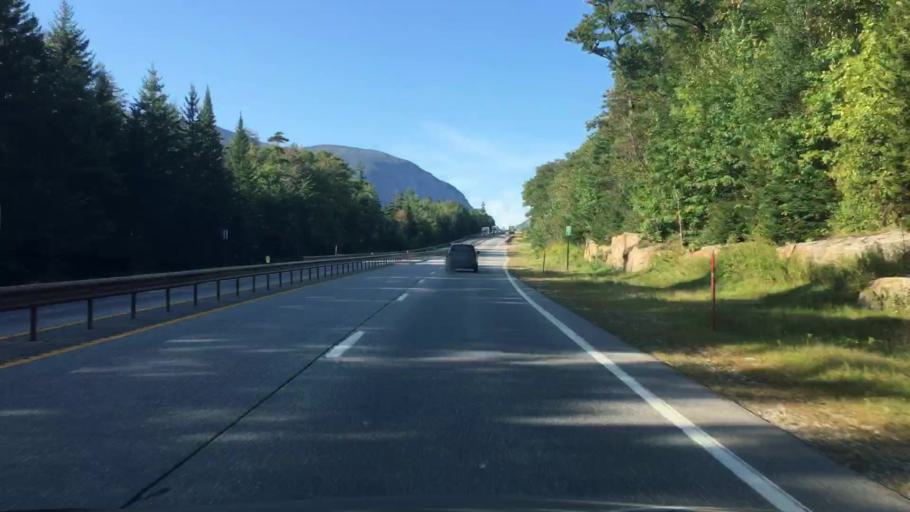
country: US
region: New Hampshire
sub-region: Grafton County
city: Deerfield
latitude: 44.1170
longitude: -71.6821
